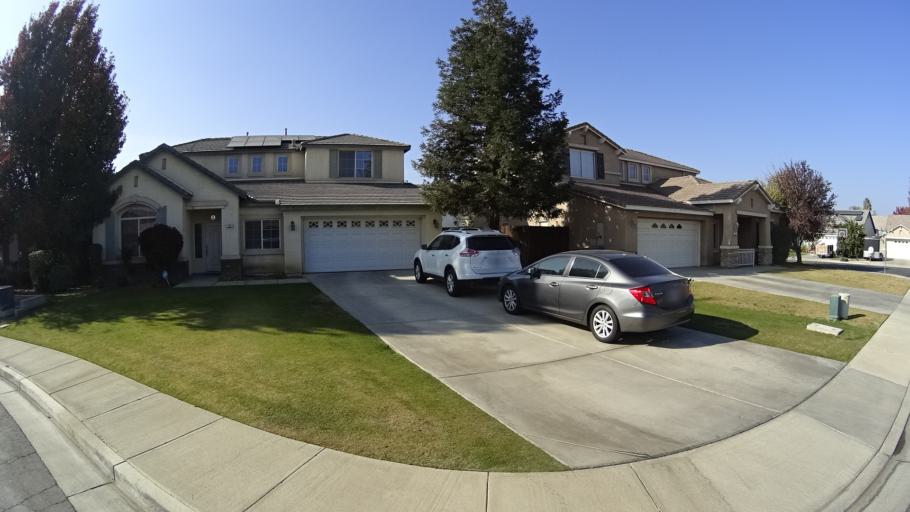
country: US
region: California
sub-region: Kern County
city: Rosedale
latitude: 35.3551
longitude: -119.1658
